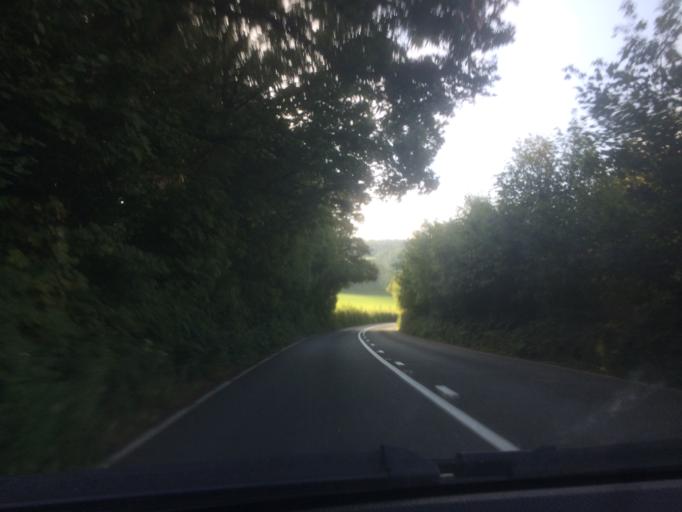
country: GB
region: England
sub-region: Cornwall
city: Gunnislake
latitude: 50.5339
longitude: -4.1994
